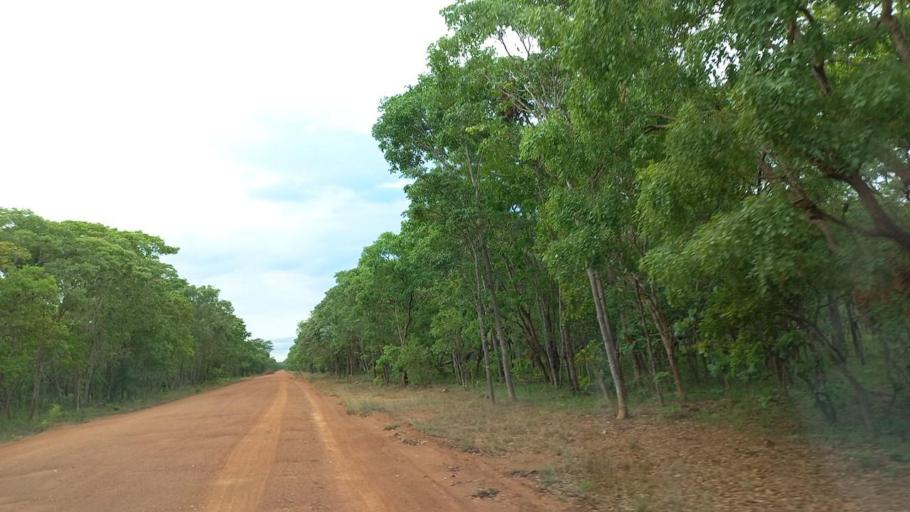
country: ZM
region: North-Western
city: Kalengwa
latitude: -13.3789
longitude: 25.0725
